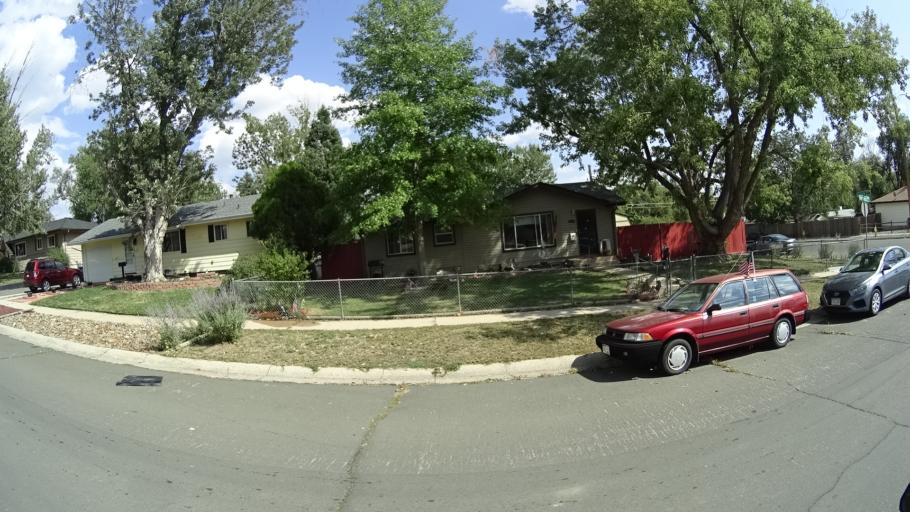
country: US
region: Colorado
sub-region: El Paso County
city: Colorado Springs
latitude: 38.8494
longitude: -104.7707
